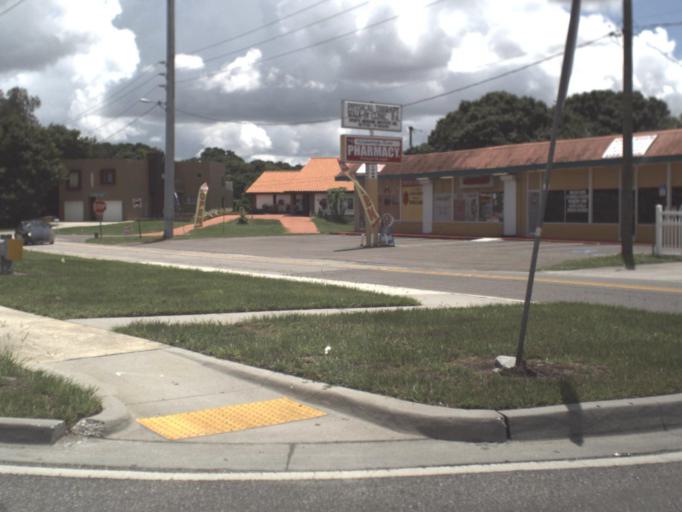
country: US
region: Florida
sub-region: Hillsborough County
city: Tampa
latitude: 27.9813
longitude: -82.4780
